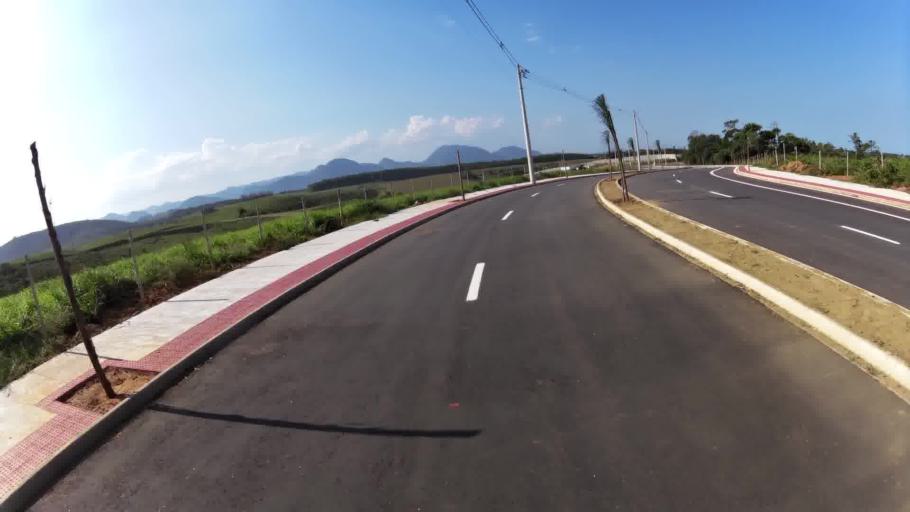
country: BR
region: Espirito Santo
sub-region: Guarapari
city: Guarapari
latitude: -20.7156
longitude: -40.5352
